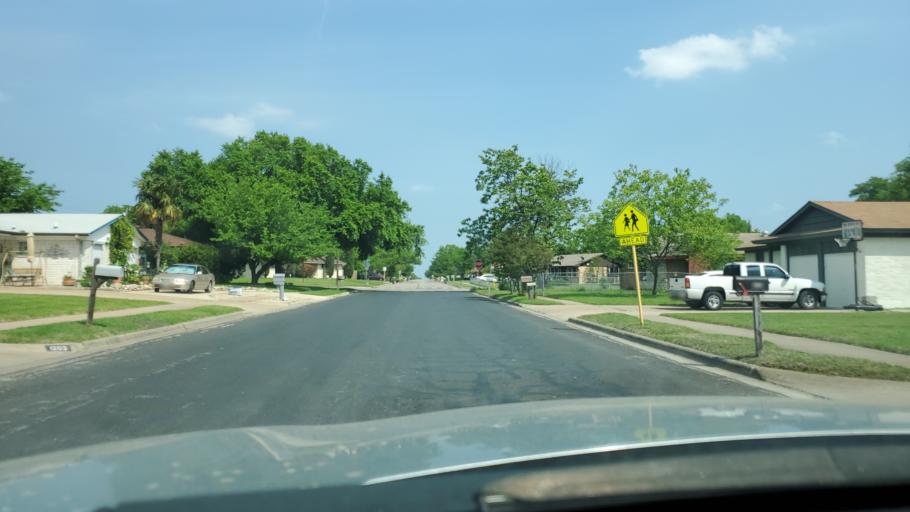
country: US
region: Texas
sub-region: Bell County
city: Killeen
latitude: 31.0984
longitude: -97.7291
